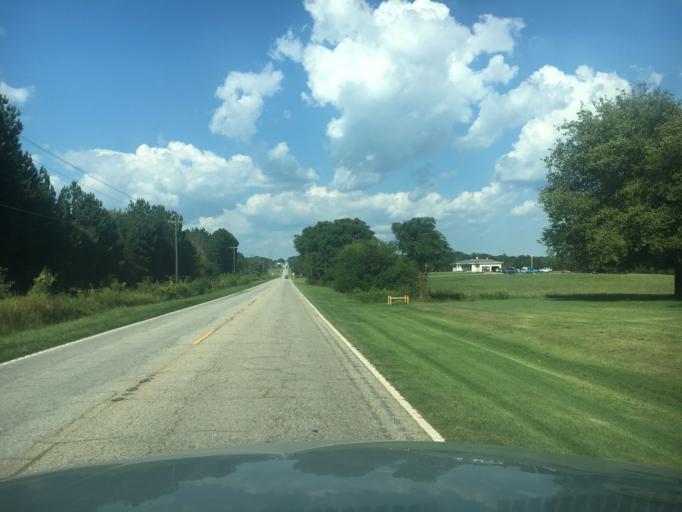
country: US
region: South Carolina
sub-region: Pickens County
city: Liberty
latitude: 34.7337
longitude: -82.6697
